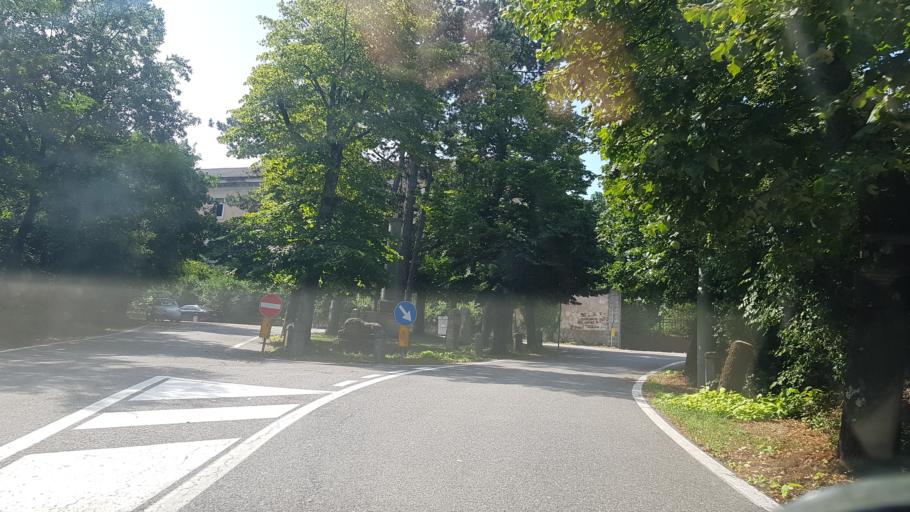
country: IT
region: Friuli Venezia Giulia
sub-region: Provincia di Trieste
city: Villa Opicina
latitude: 45.6769
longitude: 13.8045
